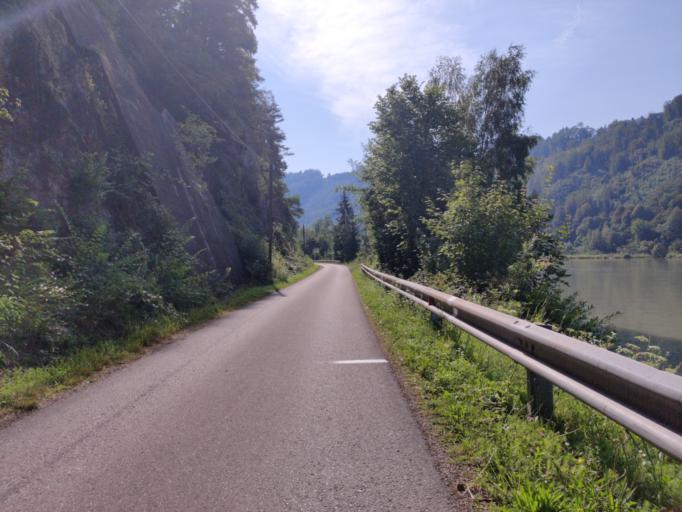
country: AT
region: Upper Austria
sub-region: Politischer Bezirk Rohrbach
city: Kleinzell im Muehlkreis
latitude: 48.4188
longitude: 13.9592
